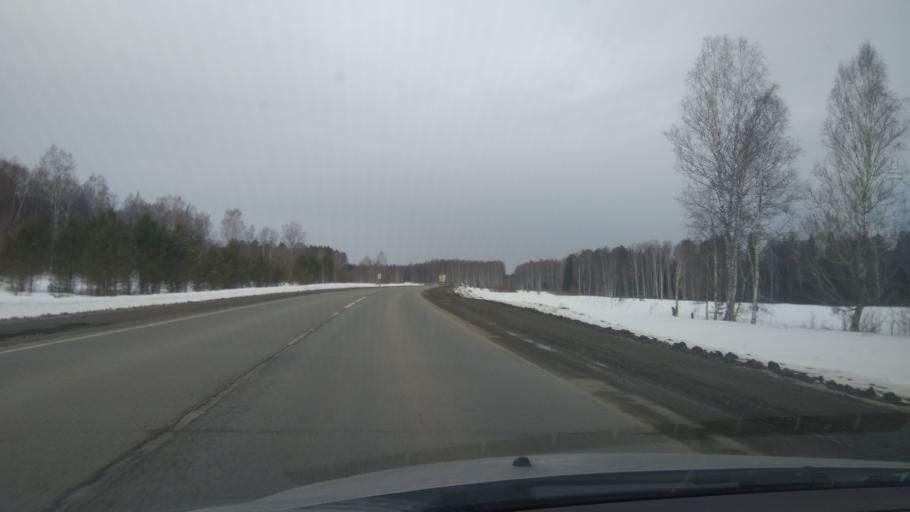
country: RU
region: Sverdlovsk
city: Ufimskiy
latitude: 56.7827
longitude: 58.3981
